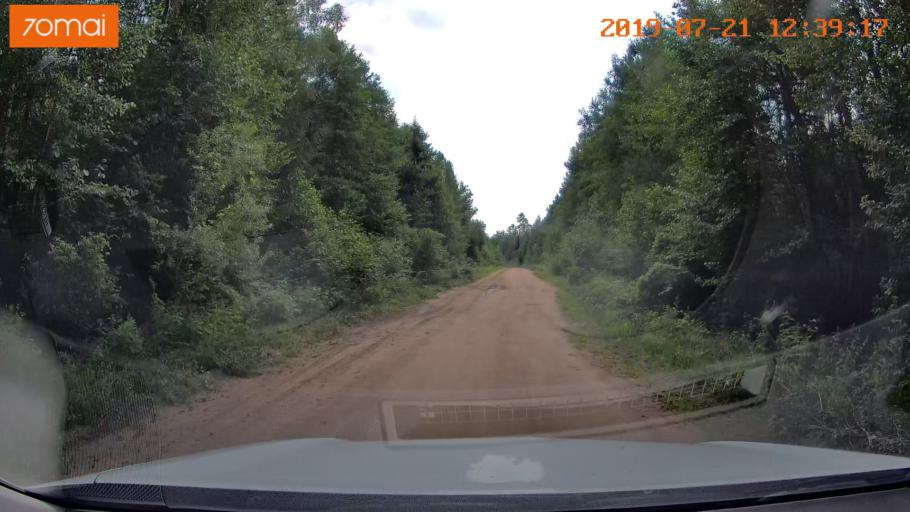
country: BY
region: Grodnenskaya
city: Lyubcha
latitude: 53.8568
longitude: 26.0164
